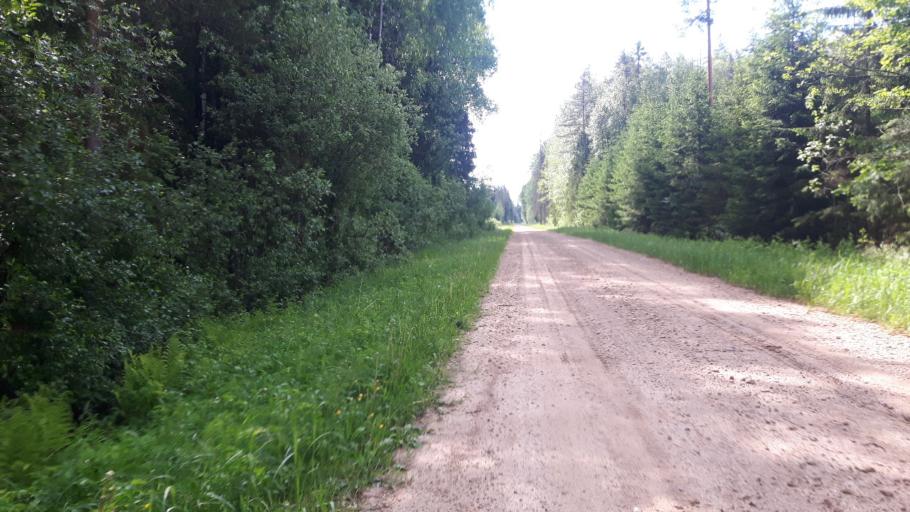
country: EE
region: Paernumaa
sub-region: Vaendra vald (alev)
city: Vandra
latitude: 58.7302
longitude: 25.0288
